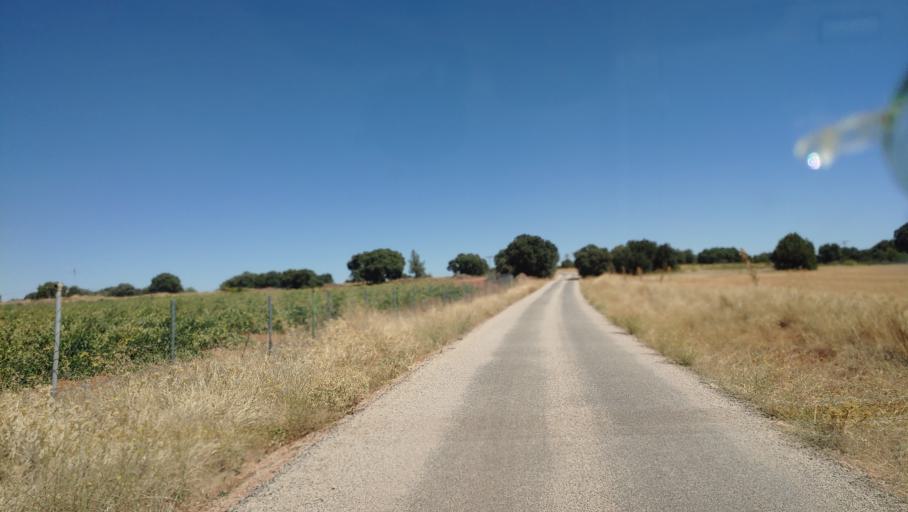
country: ES
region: Castille-La Mancha
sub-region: Provincia de Albacete
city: Ossa de Montiel
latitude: 38.9205
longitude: -2.7966
